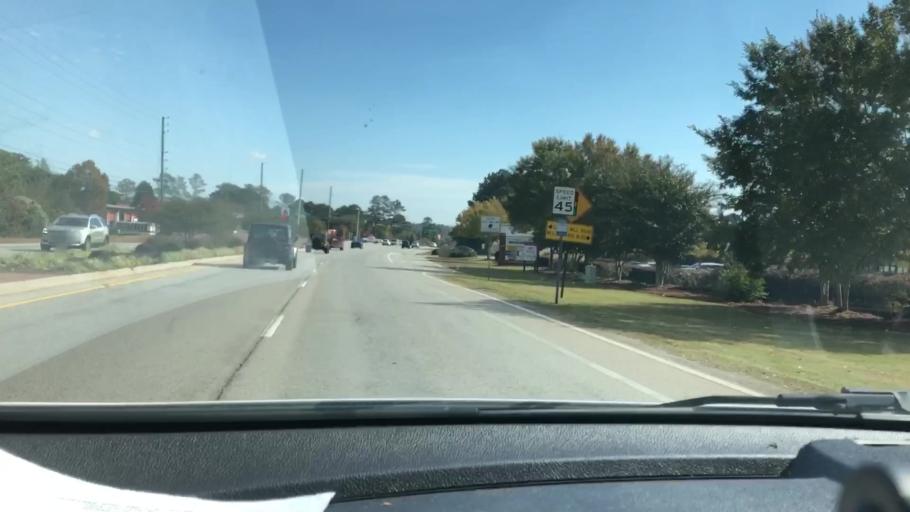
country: US
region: Georgia
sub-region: Henry County
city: McDonough
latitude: 33.4583
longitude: -84.1767
